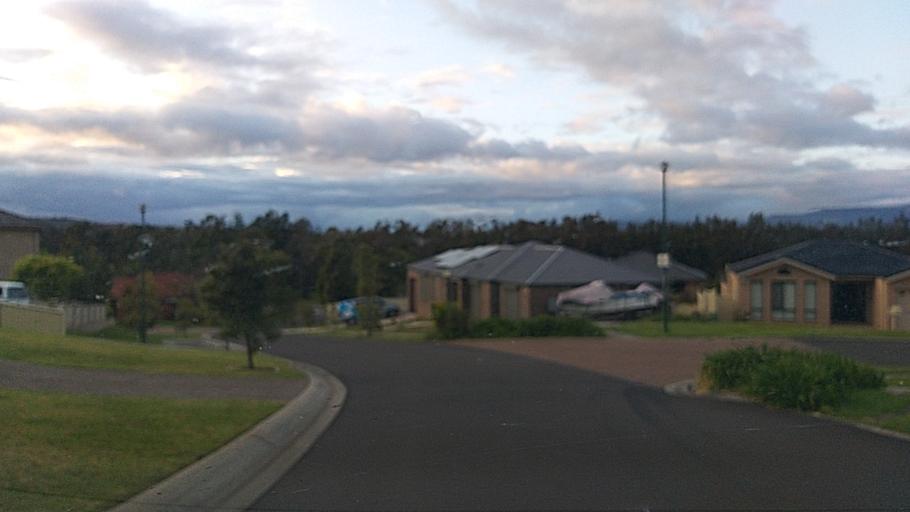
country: AU
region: New South Wales
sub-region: Wollongong
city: Dapto
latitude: -34.4942
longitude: 150.7743
